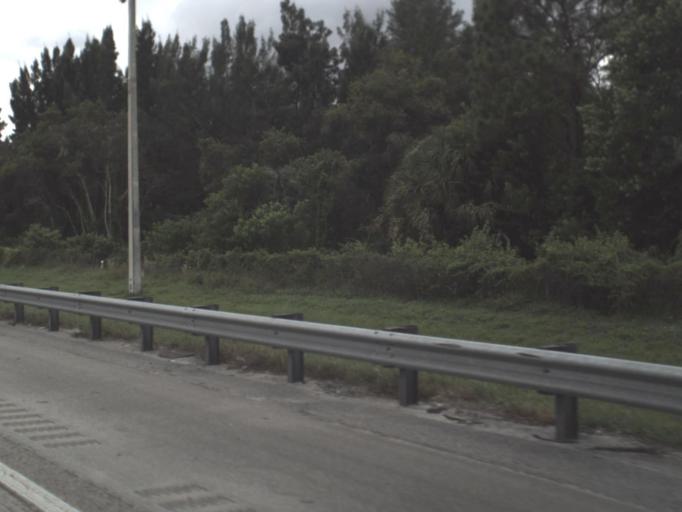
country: US
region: Florida
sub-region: Palm Beach County
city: Schall Circle
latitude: 26.7292
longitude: -80.1354
